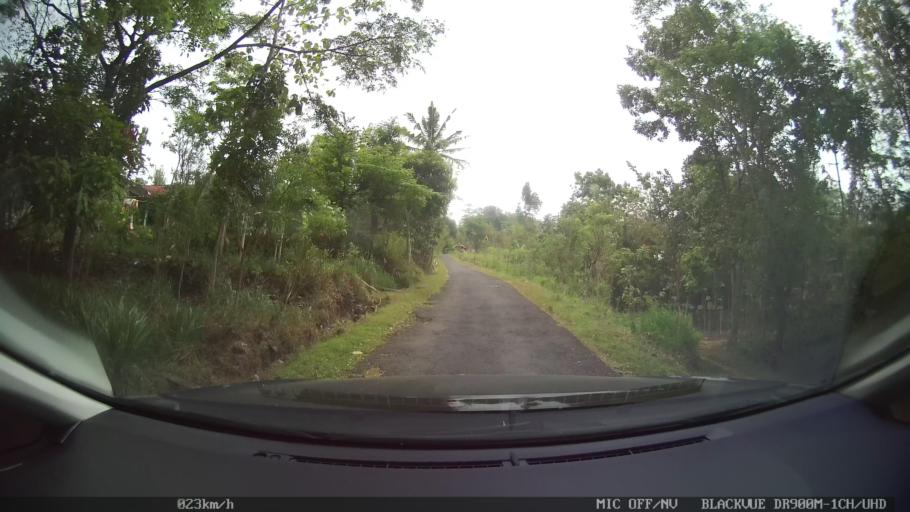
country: ID
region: Central Java
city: Candi Prambanan
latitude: -7.8048
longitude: 110.5212
